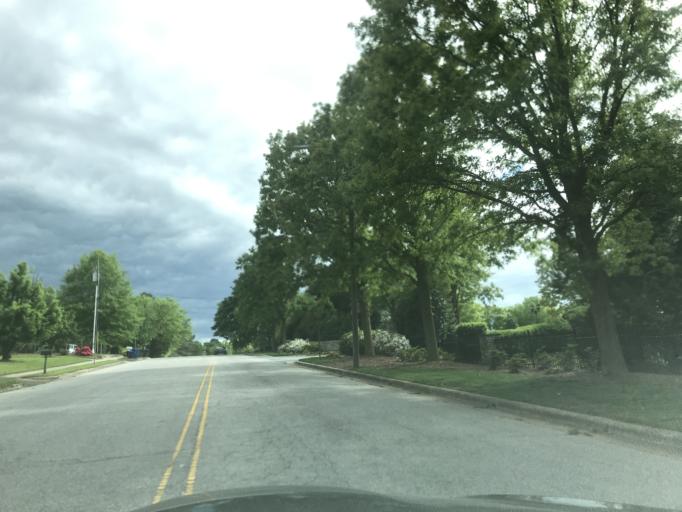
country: US
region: North Carolina
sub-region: Wake County
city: Raleigh
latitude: 35.7768
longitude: -78.5918
